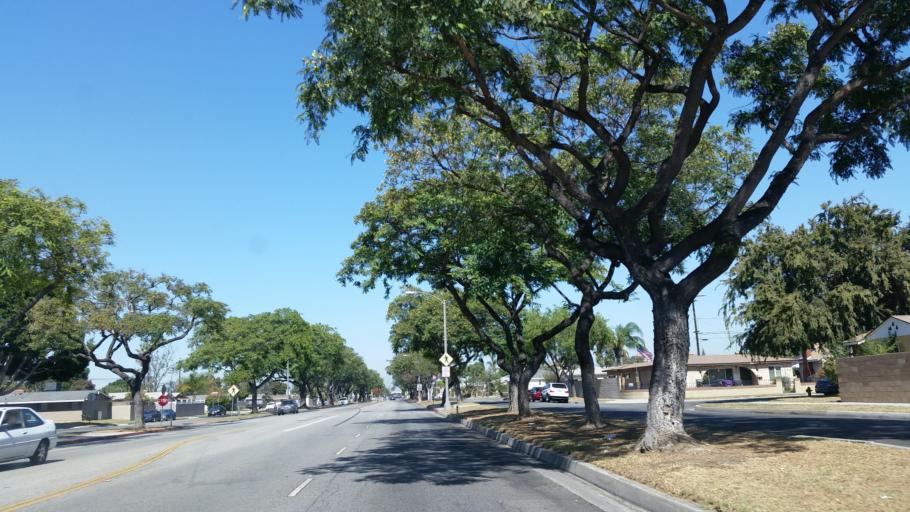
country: US
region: California
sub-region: Los Angeles County
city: Lakewood
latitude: 33.8643
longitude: -118.1512
